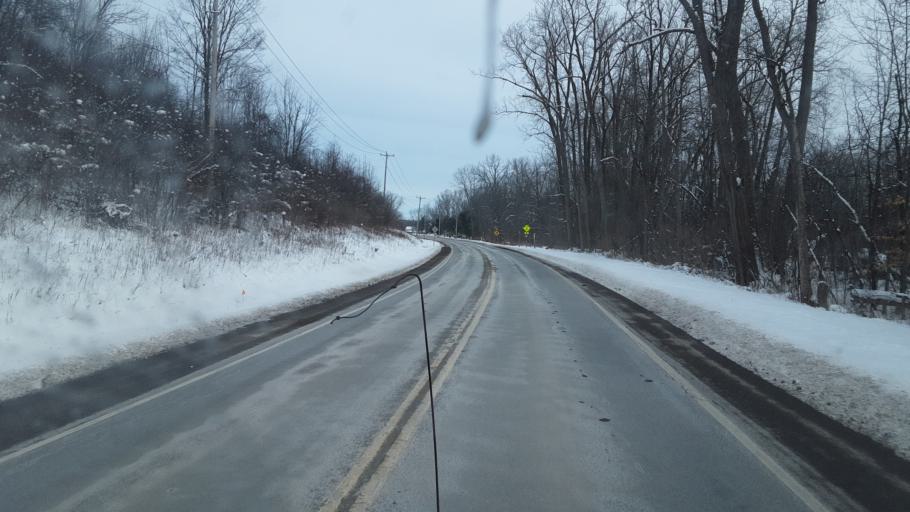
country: US
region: New York
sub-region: Wayne County
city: Newark
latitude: 43.0609
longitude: -77.0566
